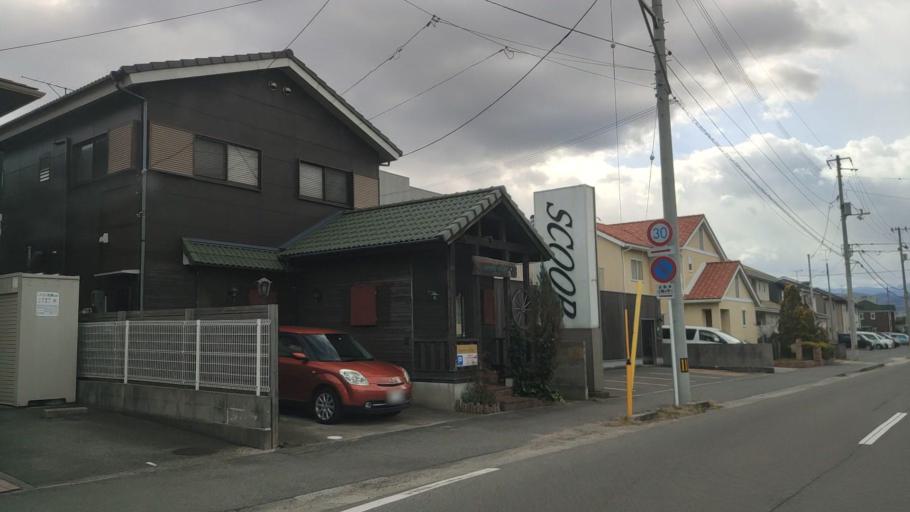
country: JP
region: Ehime
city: Saijo
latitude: 34.0448
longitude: 133.0296
